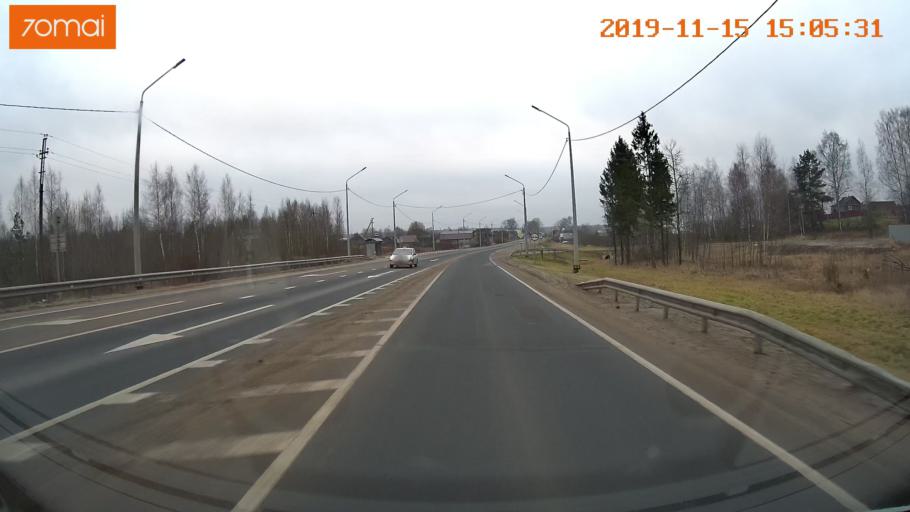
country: RU
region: Jaroslavl
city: Prechistoye
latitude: 58.4025
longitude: 40.3232
